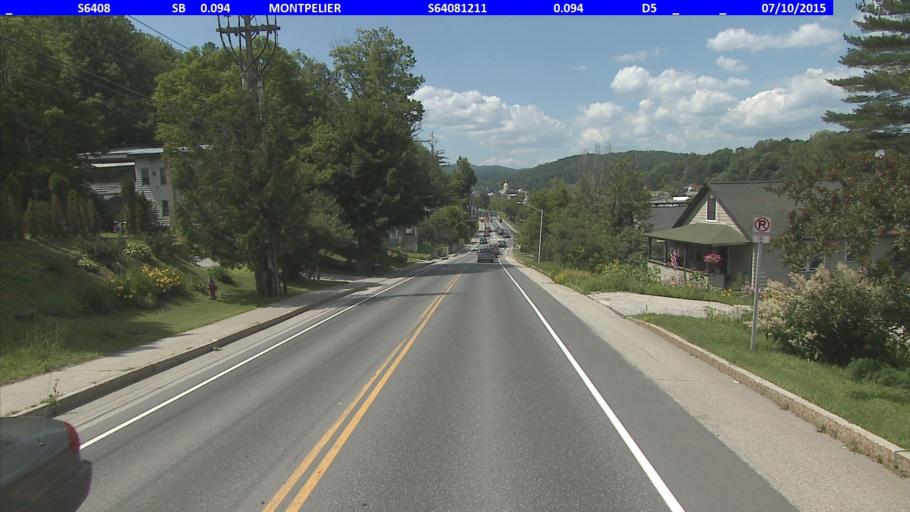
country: US
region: Vermont
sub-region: Washington County
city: Montpelier
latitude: 44.2503
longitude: -72.5704
